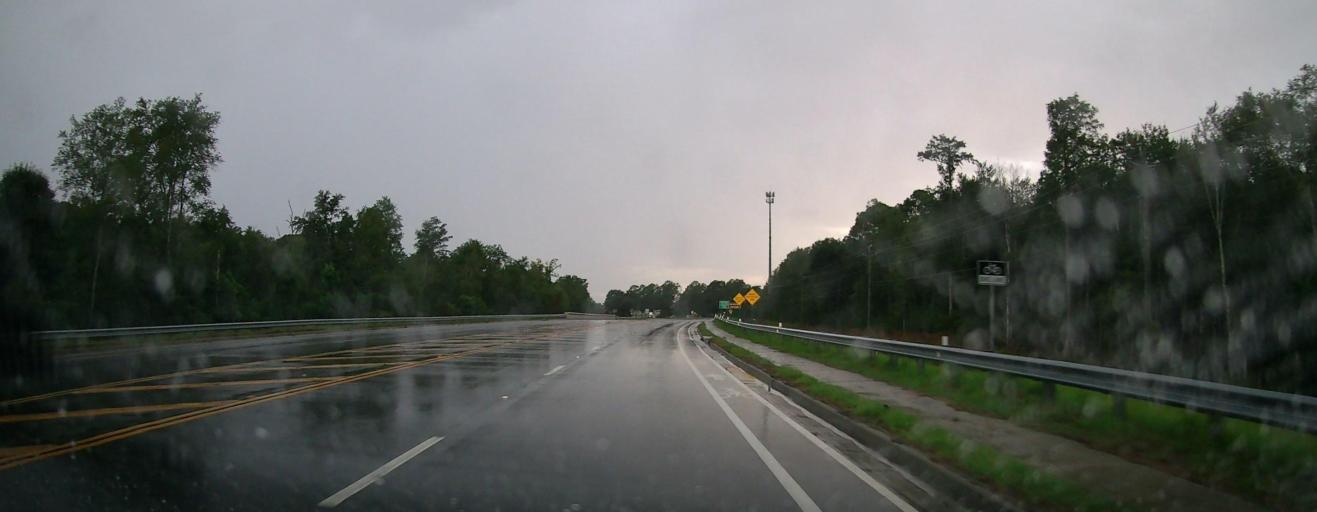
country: US
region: Georgia
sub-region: Clinch County
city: Homerville
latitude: 31.0409
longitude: -82.7350
